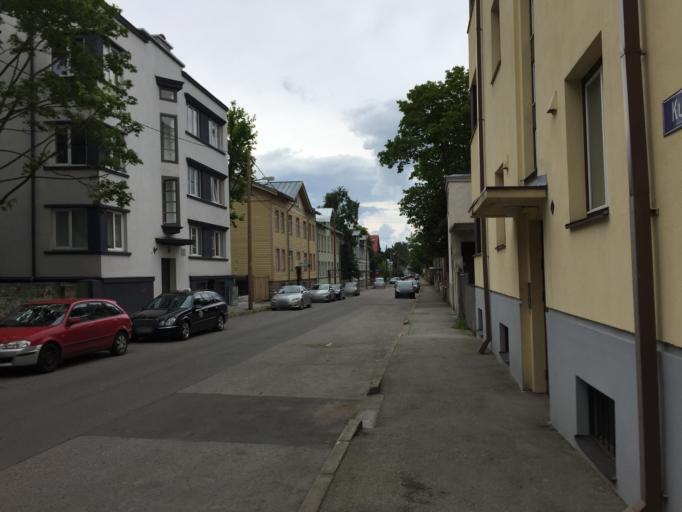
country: EE
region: Harju
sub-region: Tallinna linn
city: Tallinn
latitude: 59.4439
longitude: 24.7234
